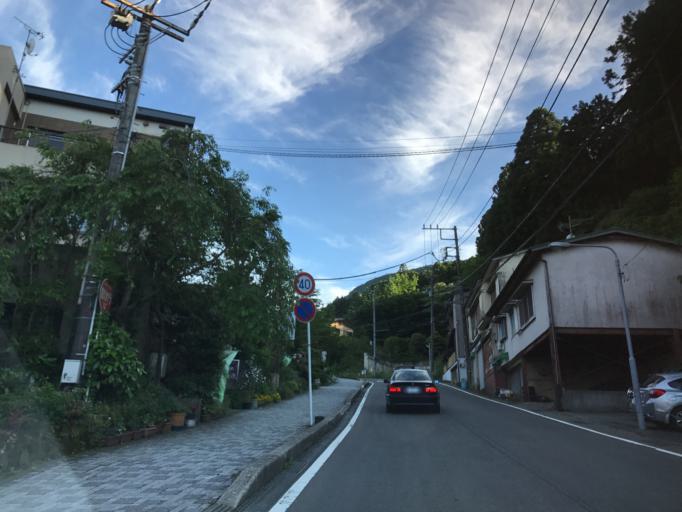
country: JP
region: Kanagawa
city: Hakone
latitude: 35.2422
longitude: 139.0495
